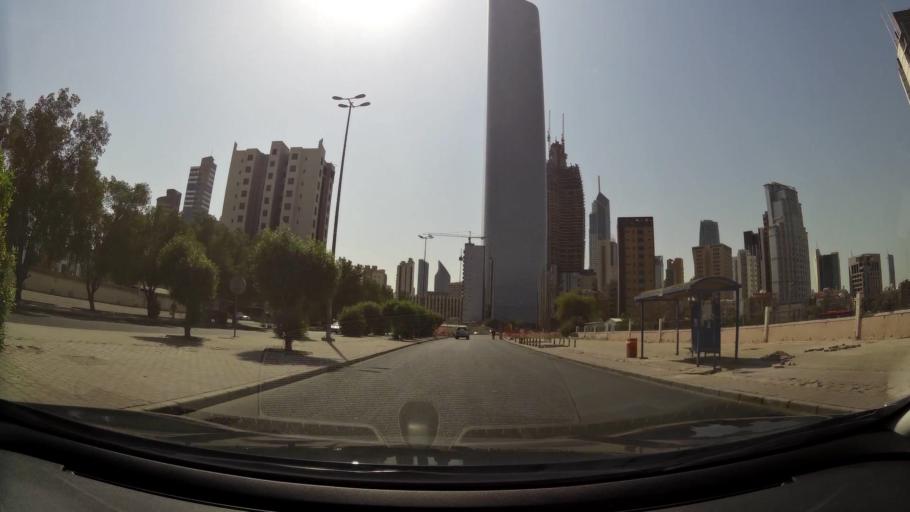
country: KW
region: Al Asimah
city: Ad Dasmah
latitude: 29.3830
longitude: 47.9943
